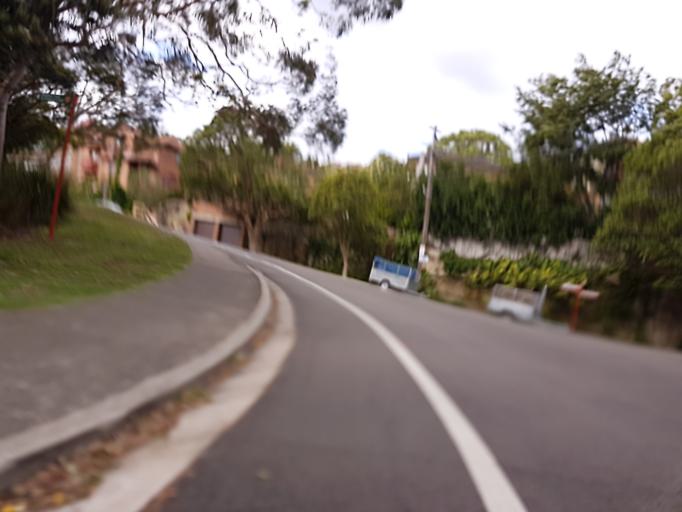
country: AU
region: New South Wales
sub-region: North Sydney
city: Cremorne
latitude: -33.8243
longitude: 151.2279
